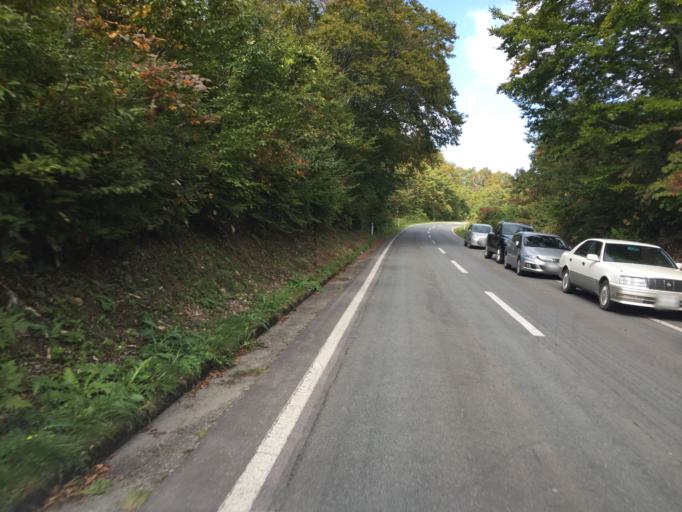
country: JP
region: Fukushima
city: Inawashiro
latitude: 37.6163
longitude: 140.0479
